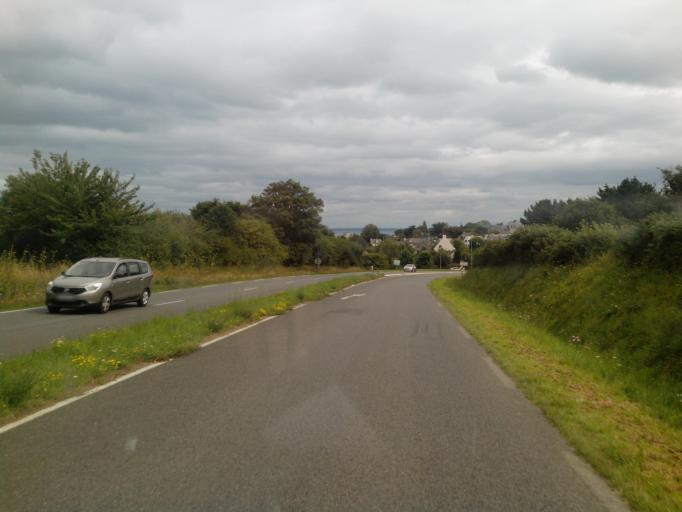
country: FR
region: Brittany
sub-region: Departement des Cotes-d'Armor
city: Saint-Quay-Portrieux
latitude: 48.6509
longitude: -2.8413
